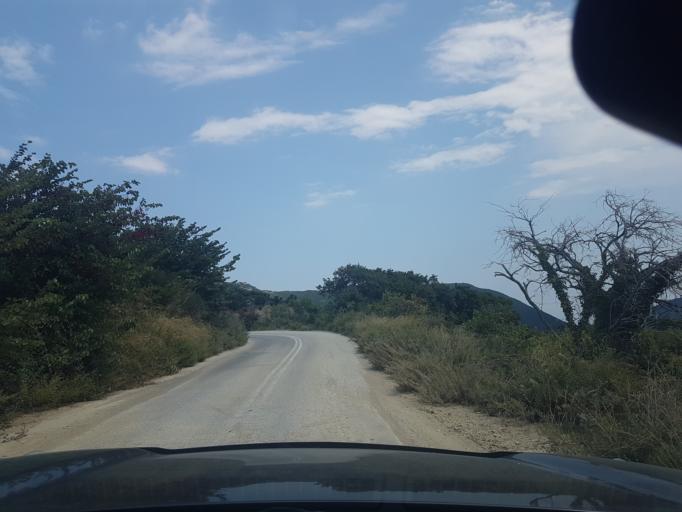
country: GR
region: Central Greece
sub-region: Nomos Evvoias
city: Kymi
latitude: 38.6450
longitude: 24.0543
